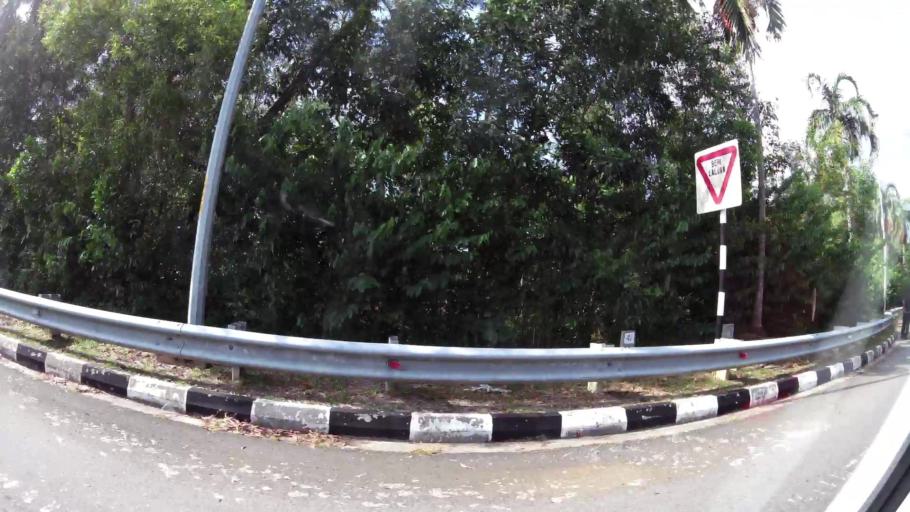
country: BN
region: Brunei and Muara
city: Bandar Seri Begawan
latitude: 4.9504
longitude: 114.9632
